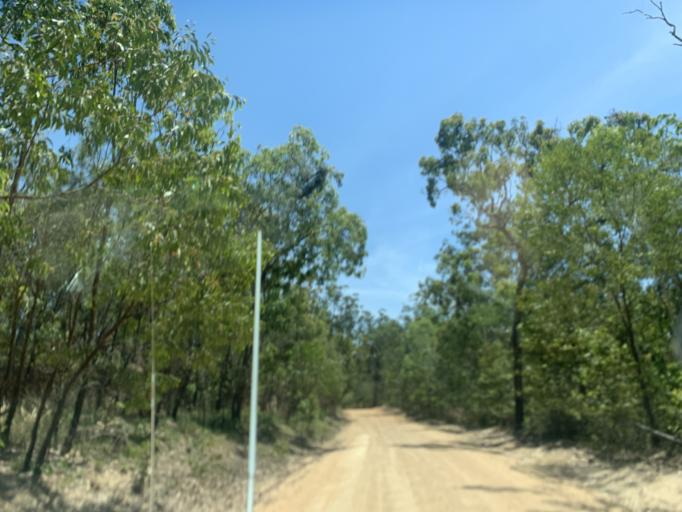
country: AU
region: Queensland
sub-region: Tablelands
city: Kuranda
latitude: -16.9183
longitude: 145.5937
